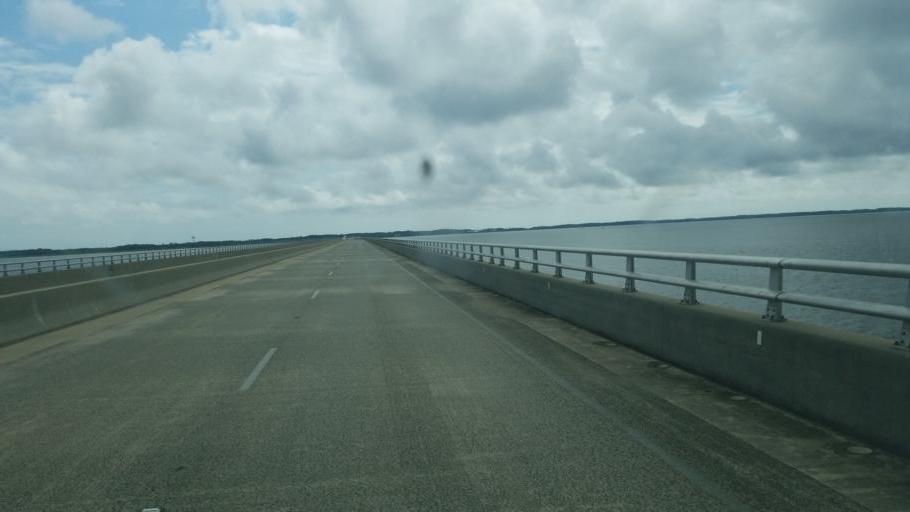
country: US
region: North Carolina
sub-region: Dare County
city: Manteo
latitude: 35.8837
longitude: -75.7009
